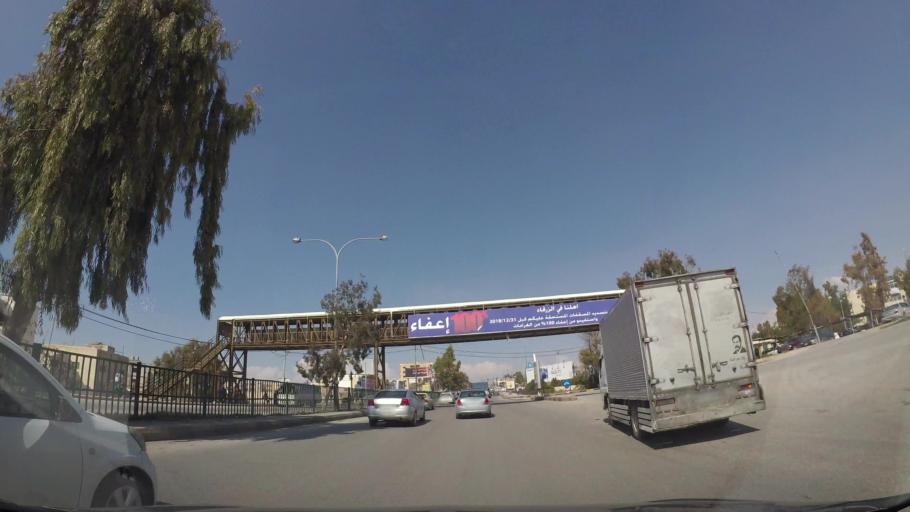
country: JO
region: Zarqa
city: Zarqa
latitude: 32.0496
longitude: 36.0925
